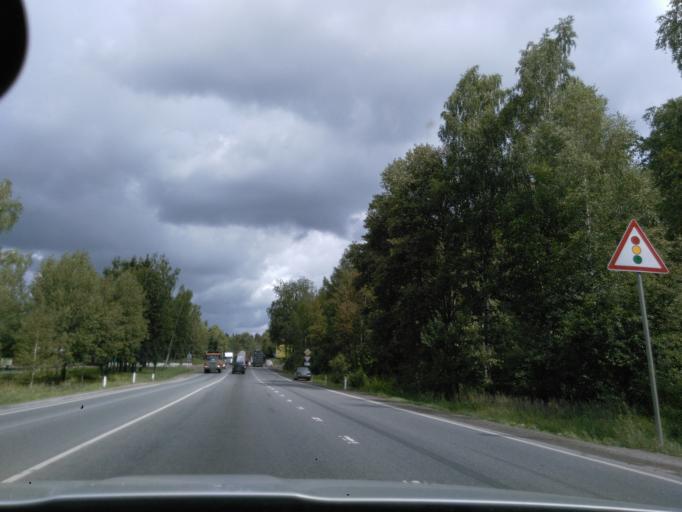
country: RU
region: Moskovskaya
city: Radumlya
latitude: 56.0591
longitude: 37.1409
